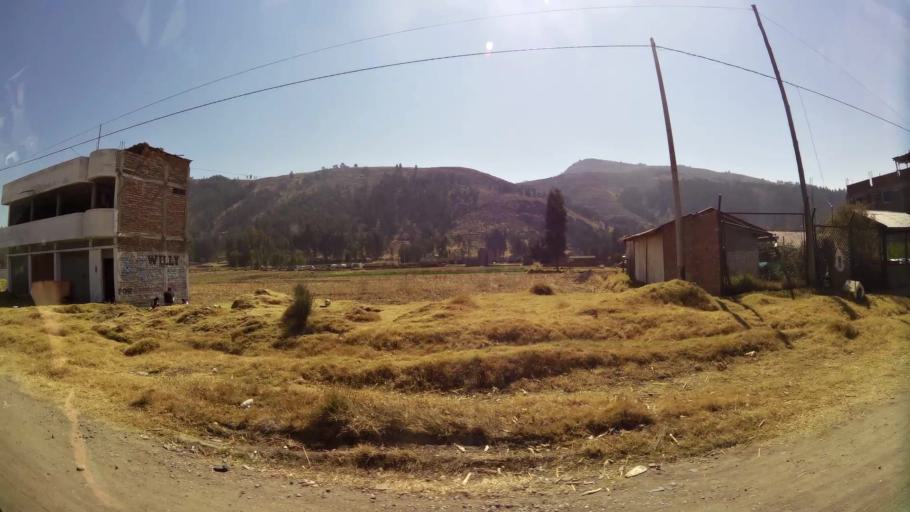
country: PE
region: Junin
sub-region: Provincia de Huancayo
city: San Jeronimo
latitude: -11.9438
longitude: -75.2959
